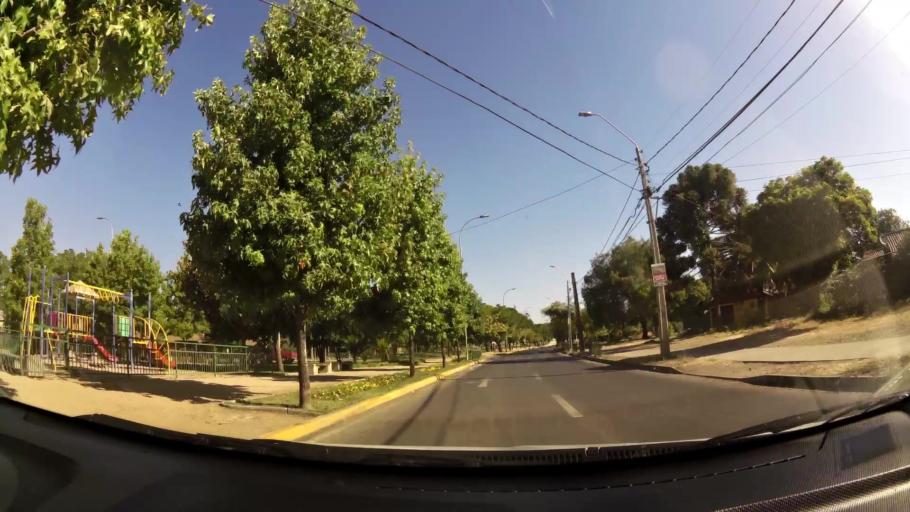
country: CL
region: Maule
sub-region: Provincia de Talca
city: Talca
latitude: -35.4267
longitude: -71.6755
